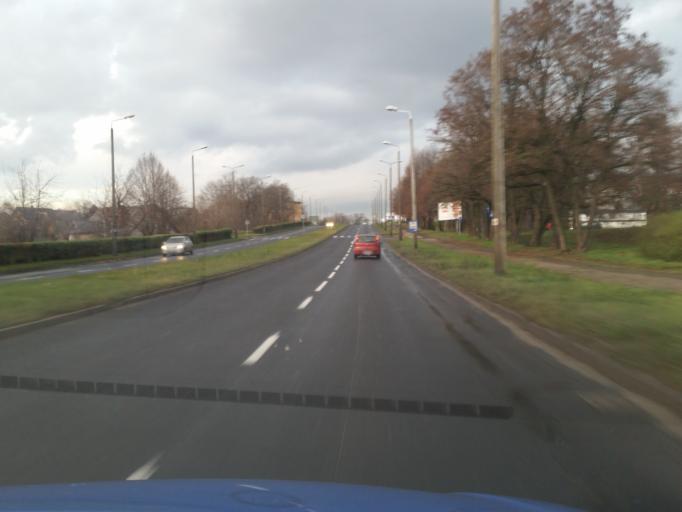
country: PL
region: Silesian Voivodeship
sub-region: Myslowice
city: Myslowice
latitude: 50.2741
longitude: 19.1766
